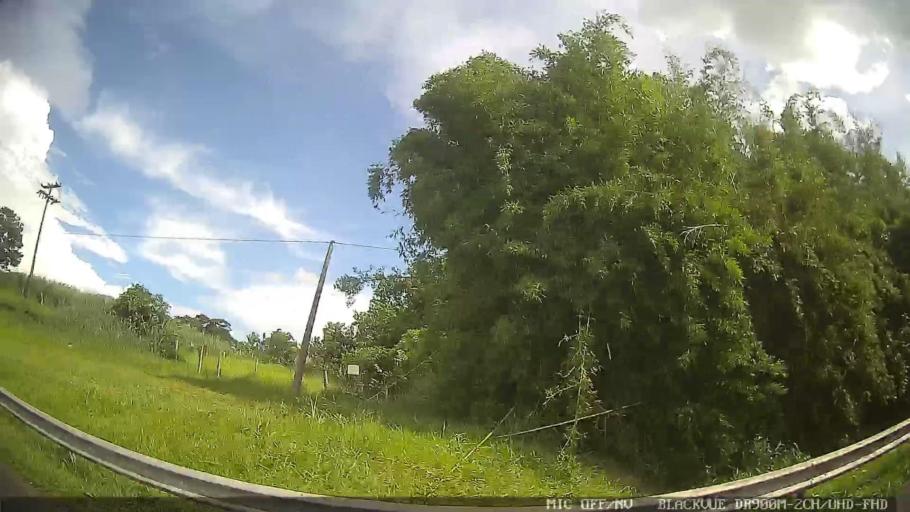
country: BR
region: Sao Paulo
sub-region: Laranjal Paulista
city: Laranjal Paulista
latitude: -23.0450
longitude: -47.9156
